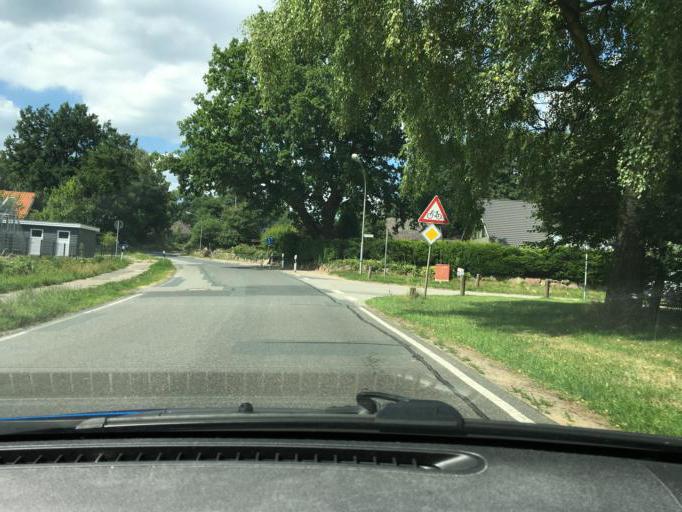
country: DE
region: Lower Saxony
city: Buchholz in der Nordheide
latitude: 53.3804
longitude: 9.8624
